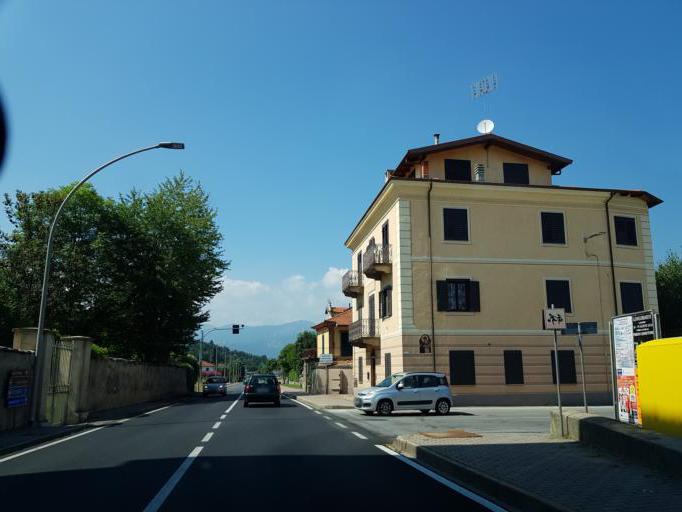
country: IT
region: Piedmont
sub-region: Provincia di Cuneo
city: Caraglio
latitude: 44.4217
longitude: 7.4316
